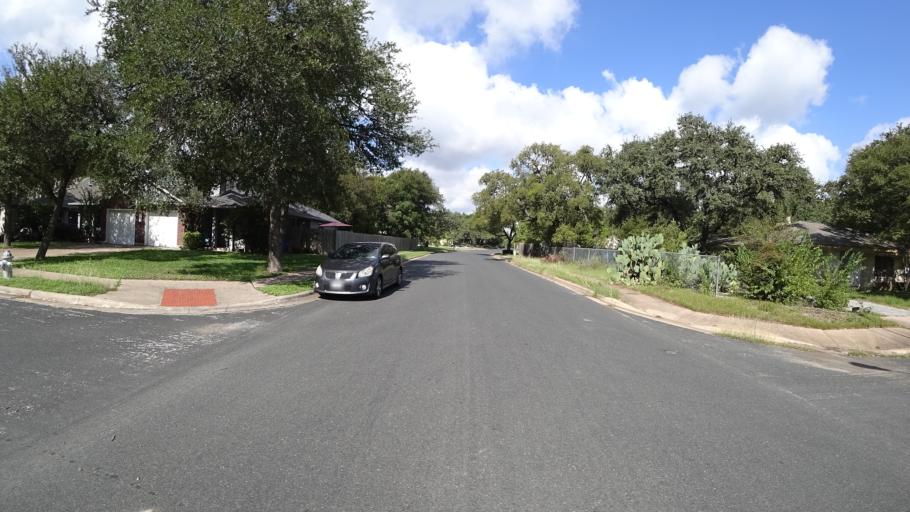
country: US
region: Texas
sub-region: Travis County
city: Shady Hollow
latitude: 30.2018
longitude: -97.8114
